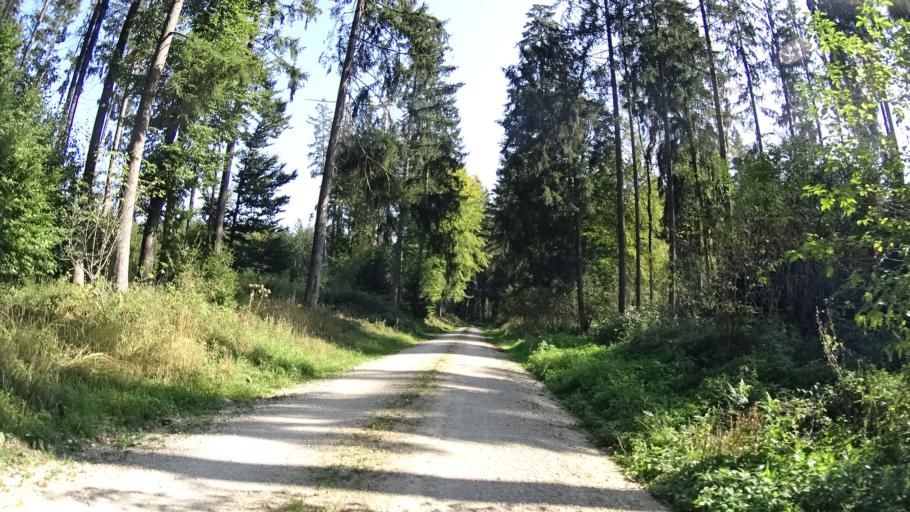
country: DE
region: Bavaria
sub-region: Upper Bavaria
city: Walting
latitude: 48.9442
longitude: 11.2553
